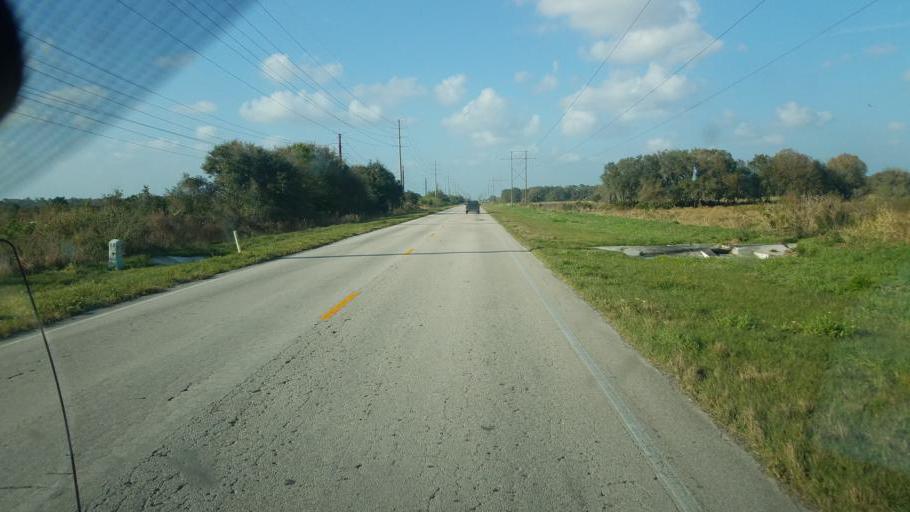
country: US
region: Florida
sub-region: Hardee County
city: Wauchula
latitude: 27.5356
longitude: -81.9290
